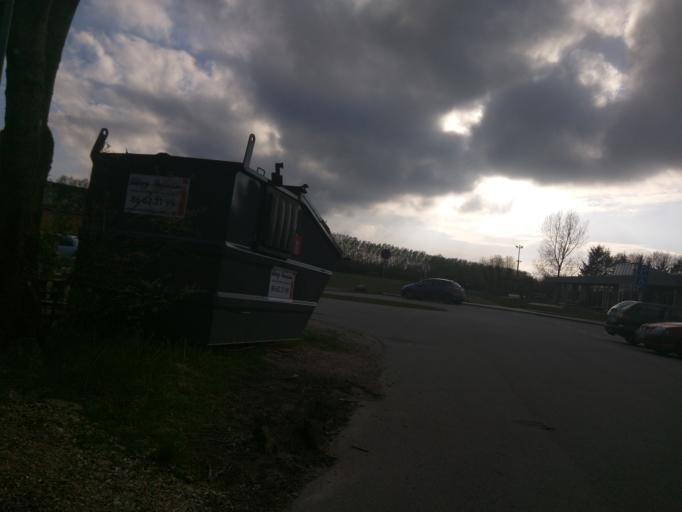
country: DK
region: Central Jutland
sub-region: Viborg Kommune
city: Viborg
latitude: 56.4415
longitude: 9.3801
